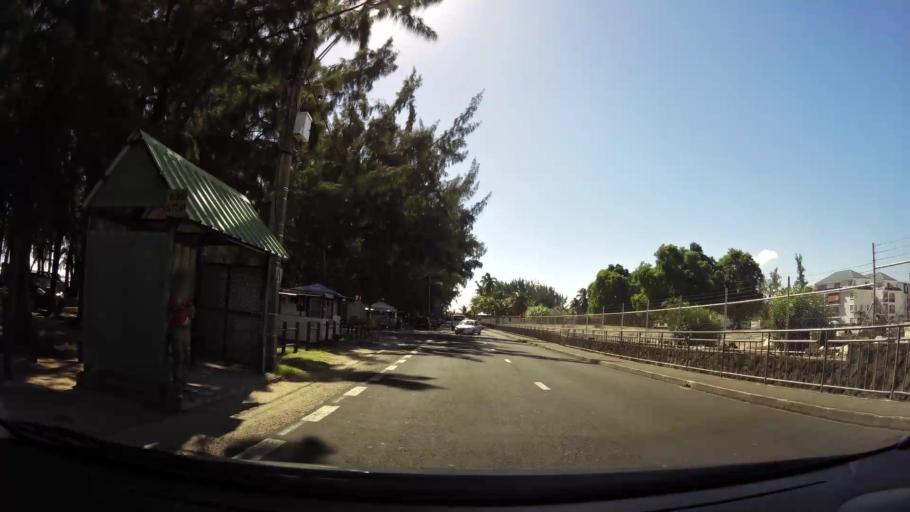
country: MU
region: Black River
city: Flic en Flac
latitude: -20.2813
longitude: 57.3658
